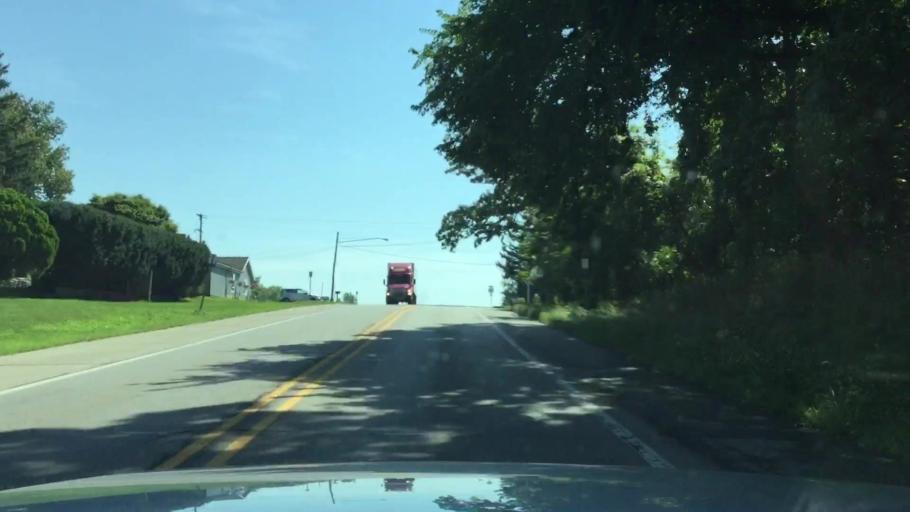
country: US
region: Michigan
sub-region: Lenawee County
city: Manitou Beach-Devils Lake
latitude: 42.0046
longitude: -84.2820
